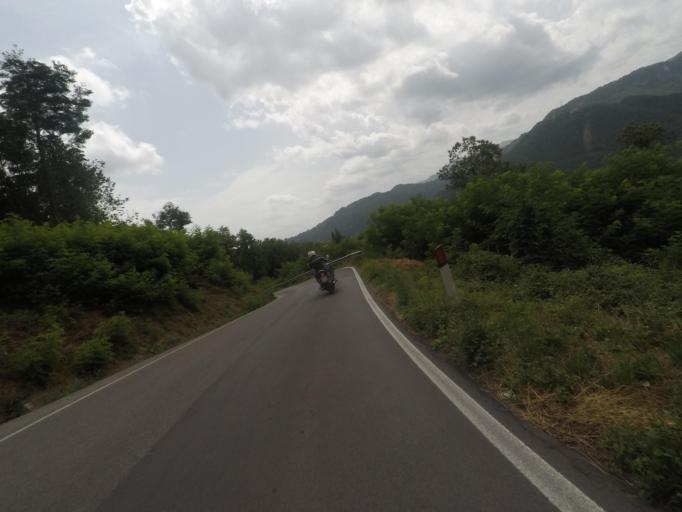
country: IT
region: Tuscany
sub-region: Provincia di Lucca
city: Castelnuovo di Garfagnana
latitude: 44.1104
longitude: 10.3914
